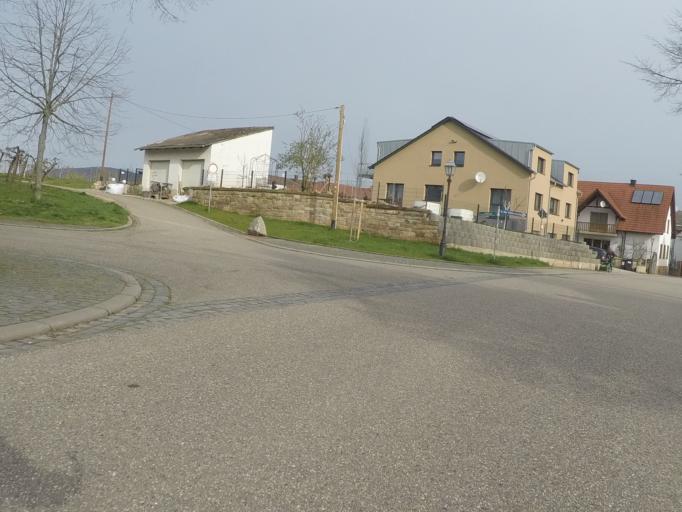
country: DE
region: Rheinland-Pfalz
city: Heuchelheim-Klingen
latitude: 49.1384
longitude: 8.0567
